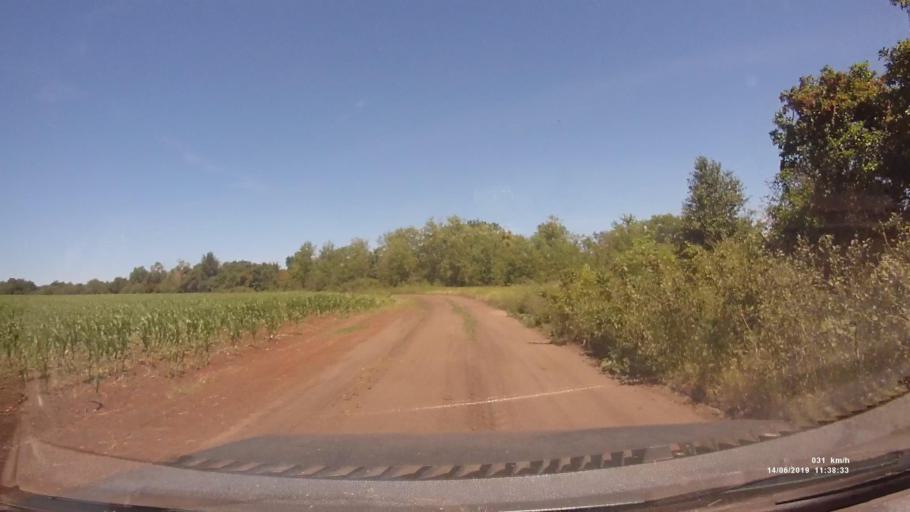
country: RU
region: Rostov
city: Kazanskaya
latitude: 49.8673
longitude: 41.3707
